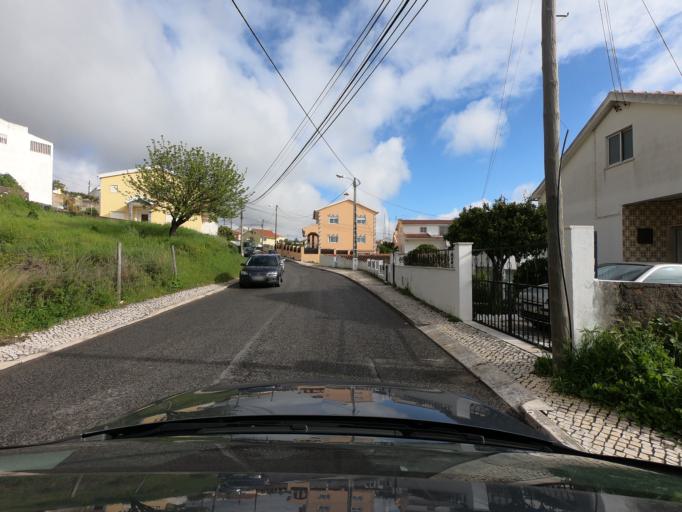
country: PT
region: Lisbon
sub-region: Oeiras
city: Porto Salvo
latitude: 38.7266
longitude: -9.3099
